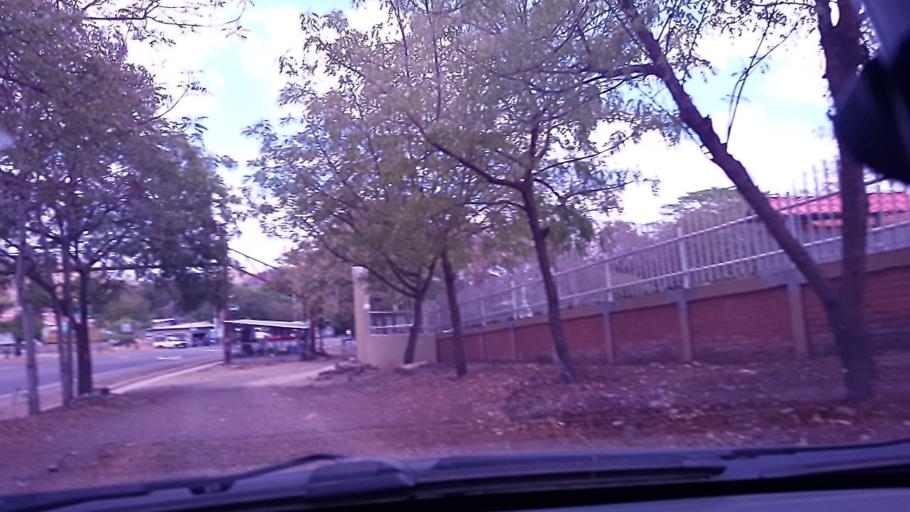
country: NI
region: Esteli
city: Condega
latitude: 13.3602
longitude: -86.4011
